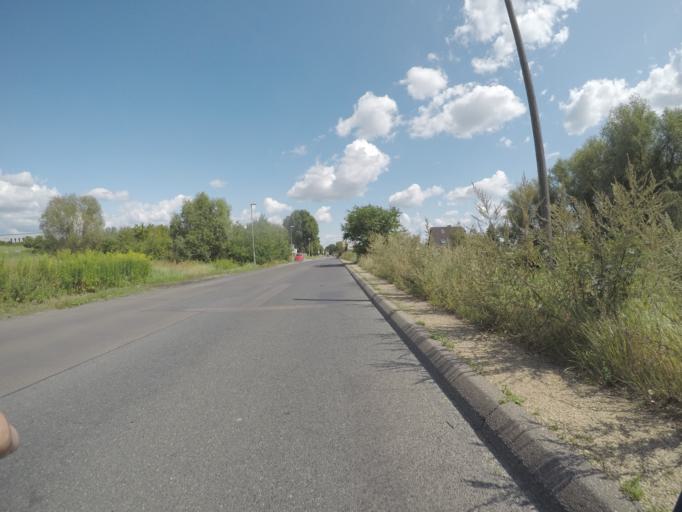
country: DE
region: Berlin
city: Mahlsdorf
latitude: 52.5012
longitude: 13.6058
